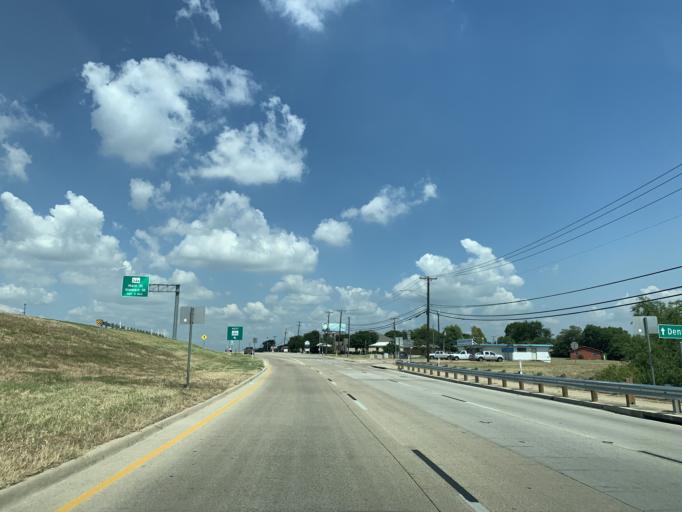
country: US
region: Texas
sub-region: Tarrant County
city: Azle
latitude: 32.8697
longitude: -97.5244
